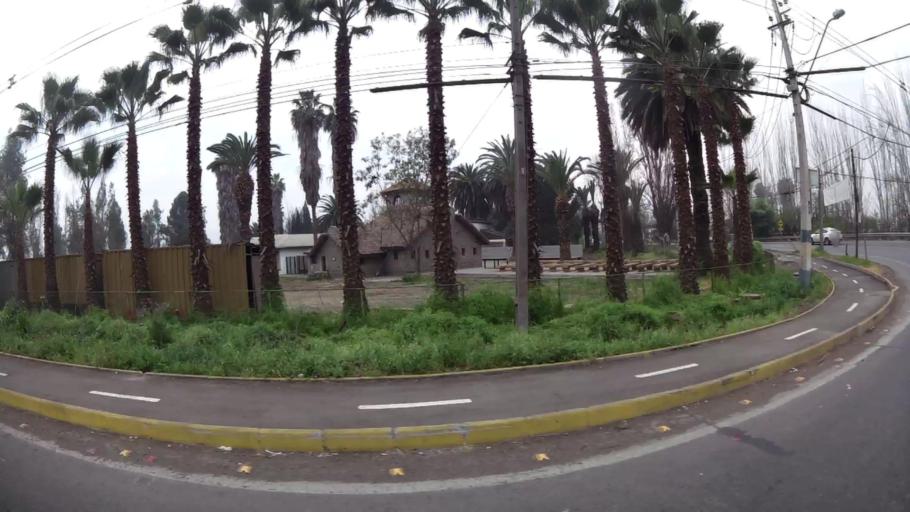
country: CL
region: Santiago Metropolitan
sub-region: Provincia de Chacabuco
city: Lampa
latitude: -33.2426
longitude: -70.7659
